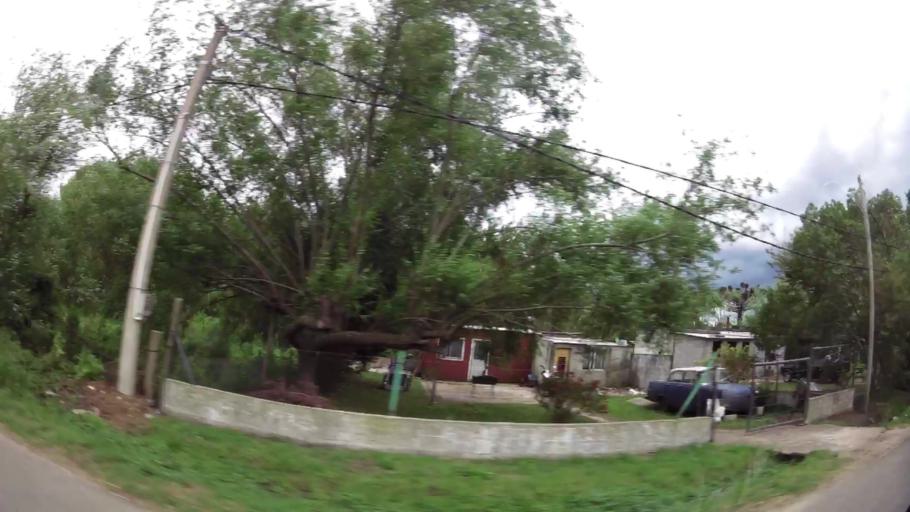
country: UY
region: Canelones
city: Toledo
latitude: -34.8014
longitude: -56.1289
